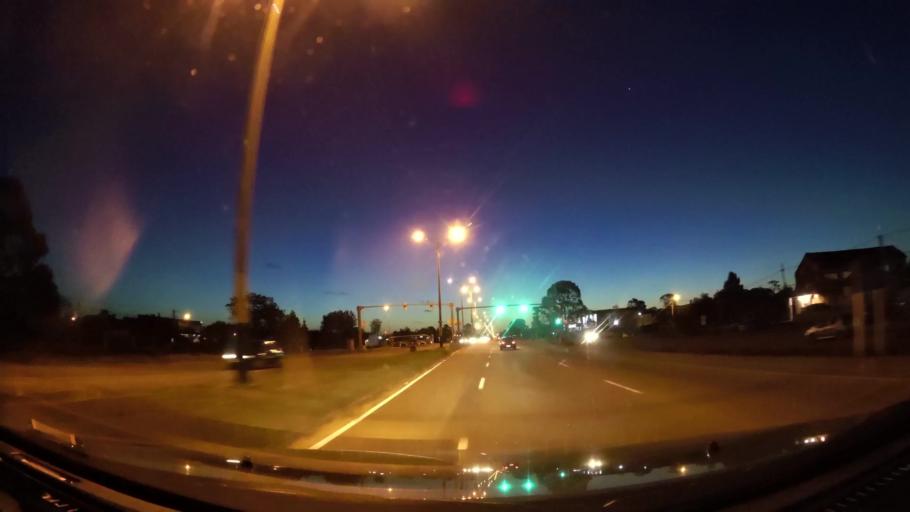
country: UY
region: Canelones
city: Colonia Nicolich
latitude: -34.8155
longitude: -55.9468
